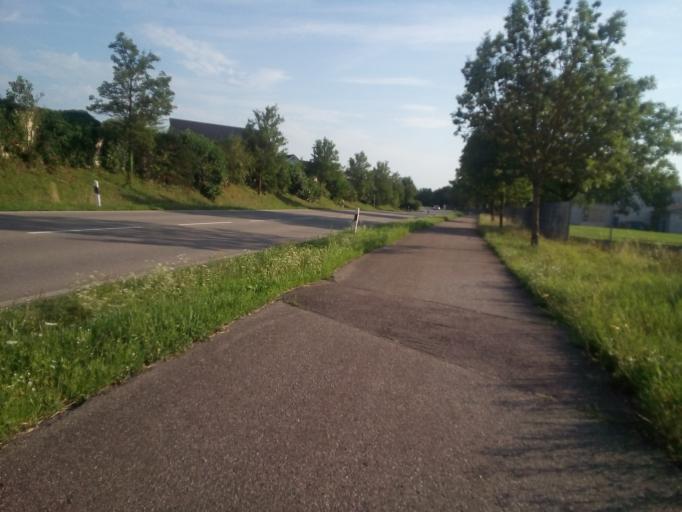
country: DE
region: Baden-Wuerttemberg
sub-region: Karlsruhe Region
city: Lichtenau
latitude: 48.7201
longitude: 7.9996
